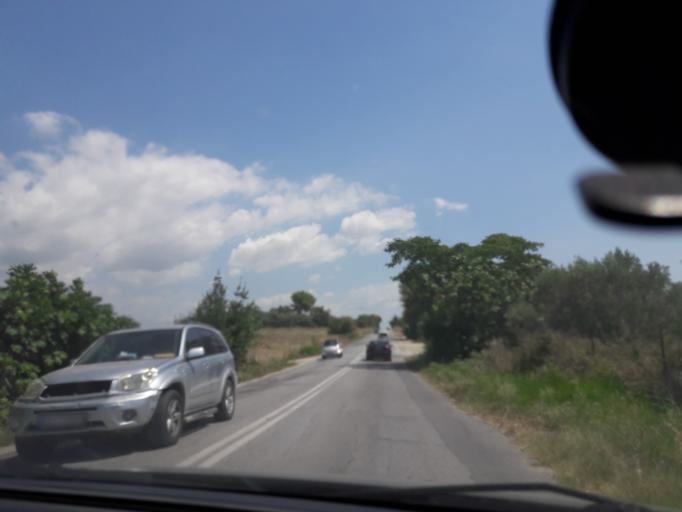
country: GR
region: Central Macedonia
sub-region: Nomos Chalkidikis
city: Nea Kallikrateia
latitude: 40.3176
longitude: 23.0735
